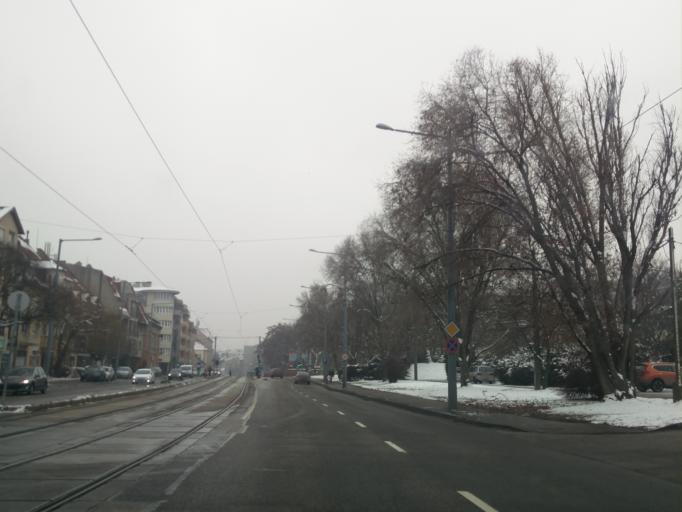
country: HU
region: Budapest
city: Budapest III. keruelet
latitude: 47.5416
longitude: 19.0304
